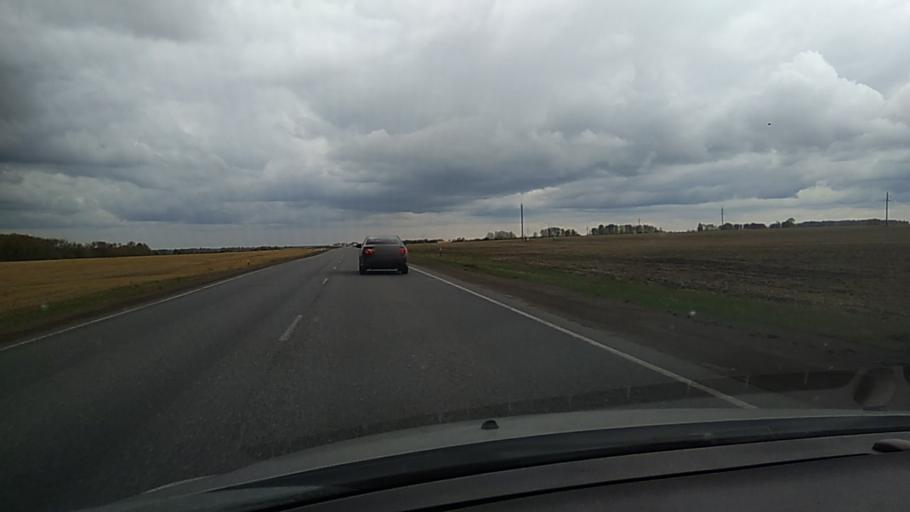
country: RU
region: Kurgan
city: Dalmatovo
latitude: 56.2896
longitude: 62.7958
